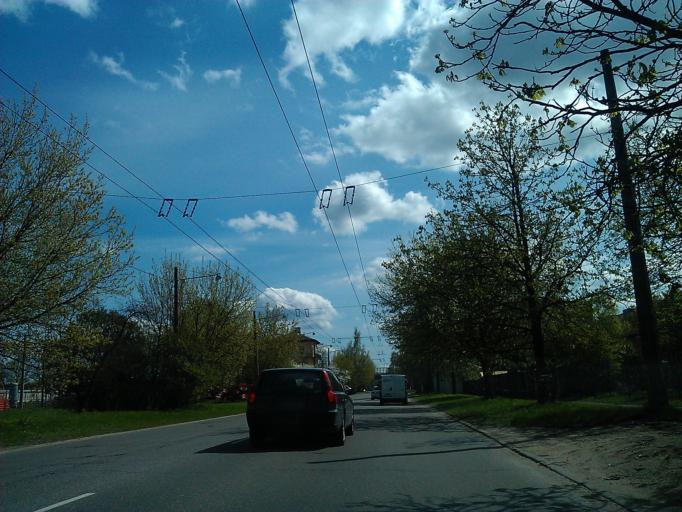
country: LV
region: Riga
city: Riga
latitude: 56.9303
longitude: 24.1712
